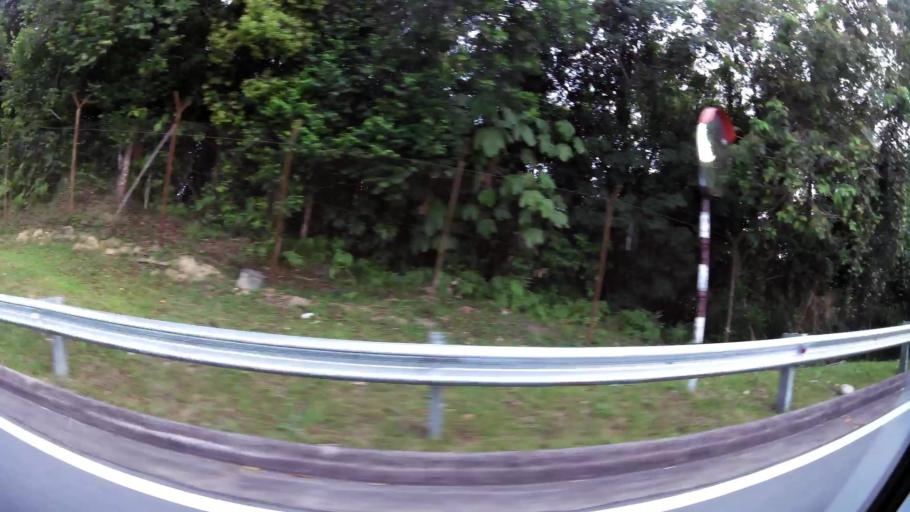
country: BN
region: Brunei and Muara
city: Bandar Seri Begawan
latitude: 4.9137
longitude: 114.9013
